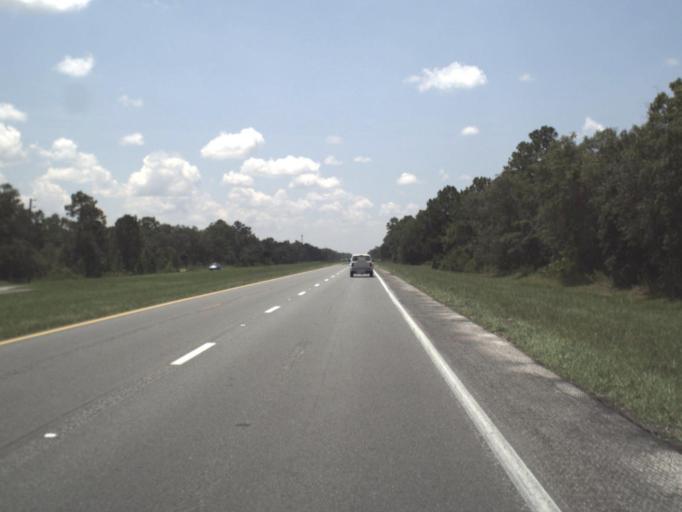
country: US
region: Florida
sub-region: Hernando County
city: North Weeki Wachee
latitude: 28.6435
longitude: -82.5522
